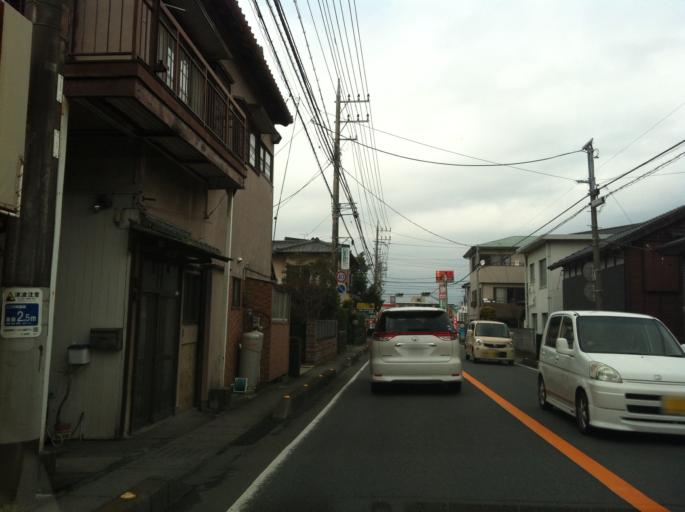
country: JP
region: Shizuoka
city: Numazu
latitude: 35.0747
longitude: 138.8730
